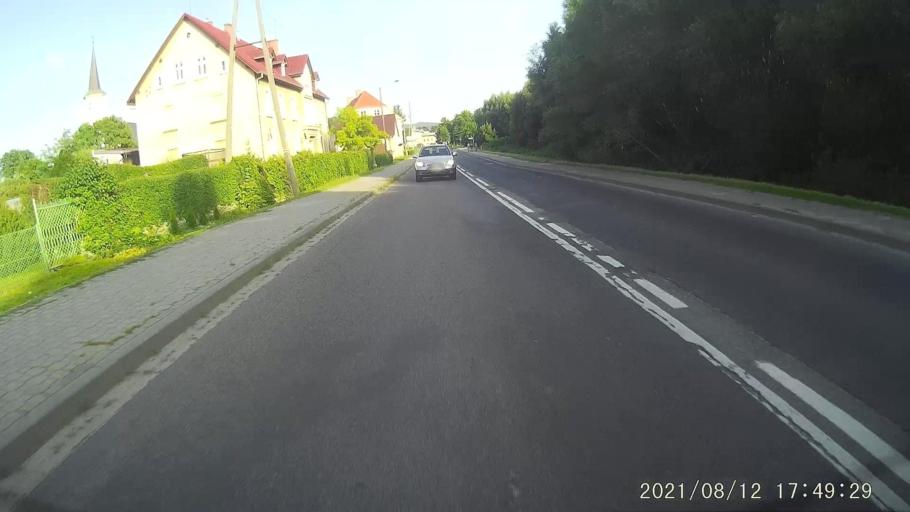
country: PL
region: Lower Silesian Voivodeship
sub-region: Powiat klodzki
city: Klodzko
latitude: 50.3609
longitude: 16.7189
